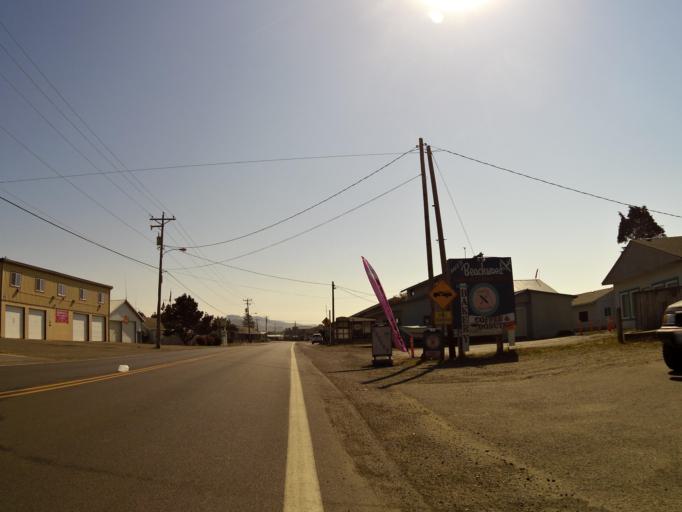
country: US
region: Oregon
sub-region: Tillamook County
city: Pacific City
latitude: 45.2016
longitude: -123.9617
